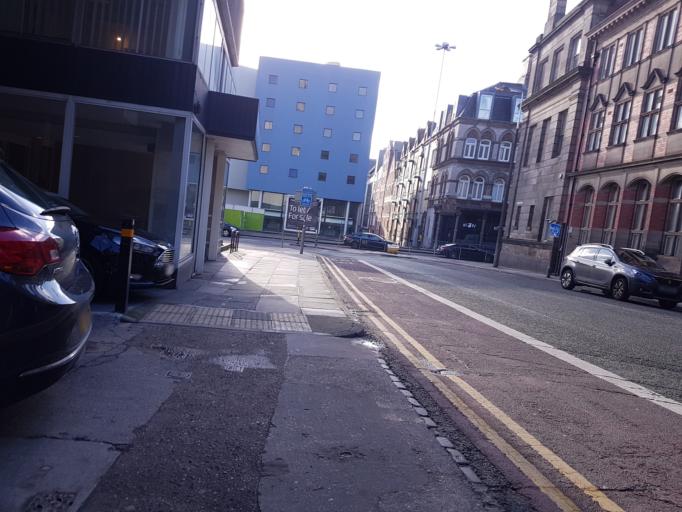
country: GB
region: England
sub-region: Liverpool
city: Liverpool
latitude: 53.4095
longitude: -2.9857
